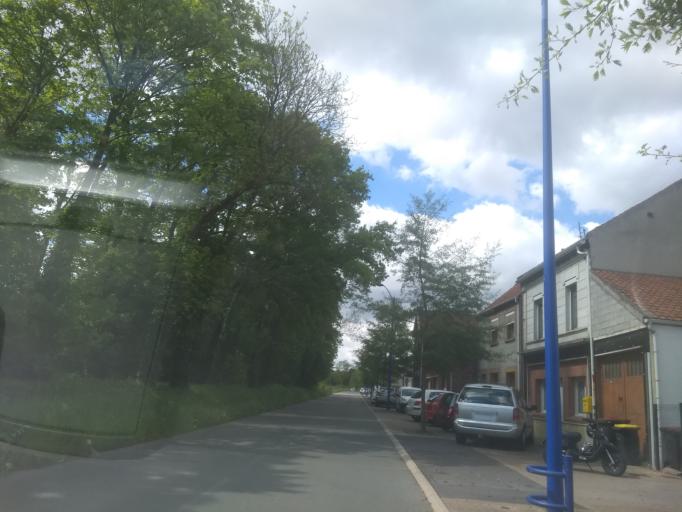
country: FR
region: Nord-Pas-de-Calais
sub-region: Departement du Pas-de-Calais
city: Drocourt
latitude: 50.4029
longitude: 2.9232
